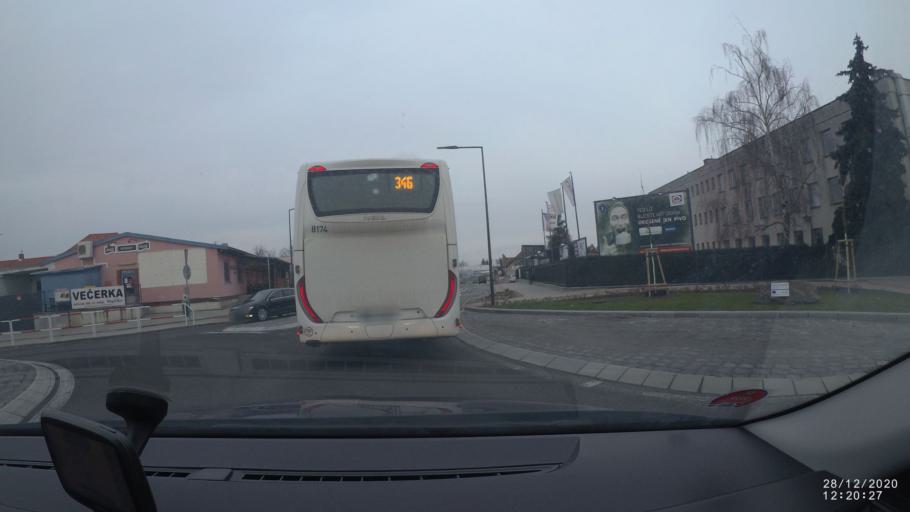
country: CZ
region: Central Bohemia
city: Brandys nad Labem-Stara Boleslav
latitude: 50.1775
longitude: 14.6533
